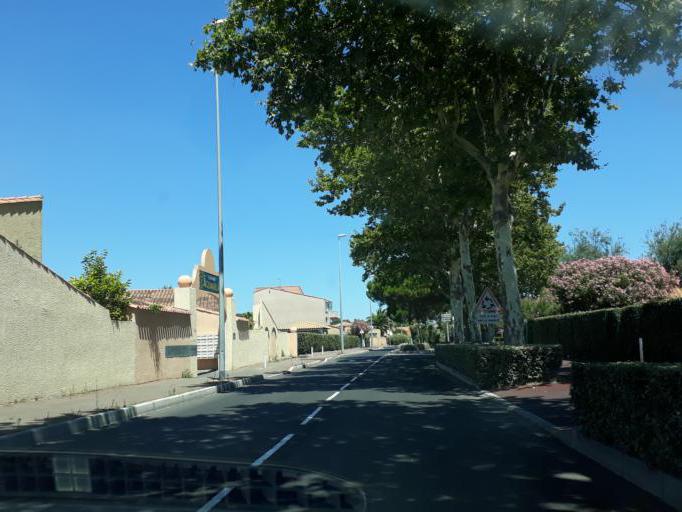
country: FR
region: Languedoc-Roussillon
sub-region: Departement de l'Herault
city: Le Cap d'Agde
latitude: 43.2794
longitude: 3.4910
